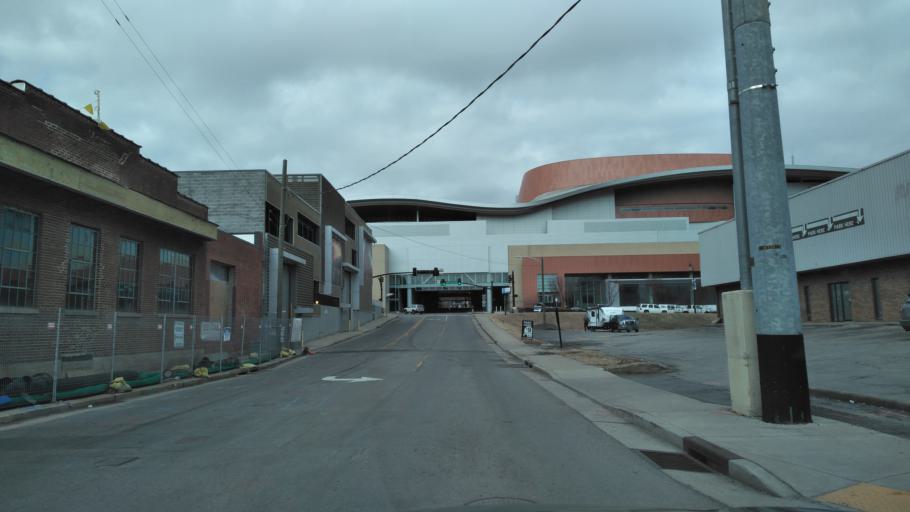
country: US
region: Tennessee
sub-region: Davidson County
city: Nashville
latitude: 36.1549
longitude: -86.7766
